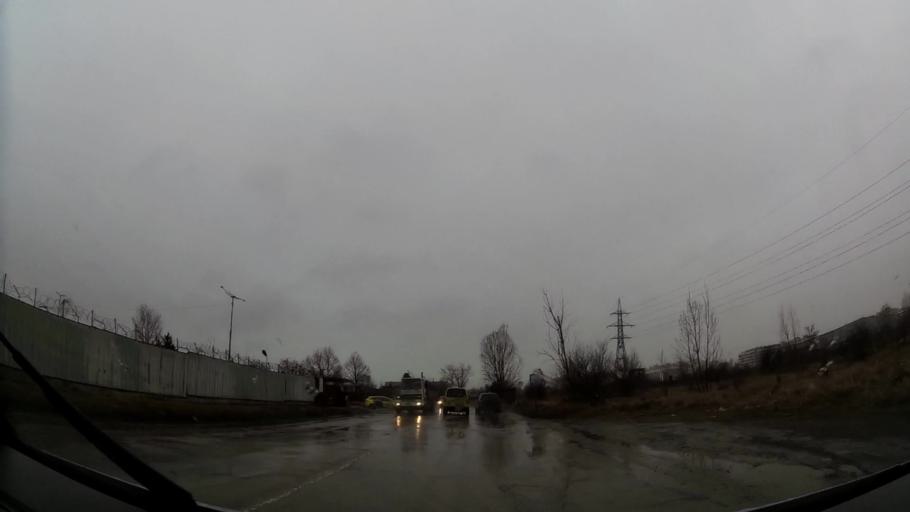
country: BG
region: Sofia-Capital
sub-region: Stolichna Obshtina
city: Sofia
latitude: 42.6498
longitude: 23.4136
